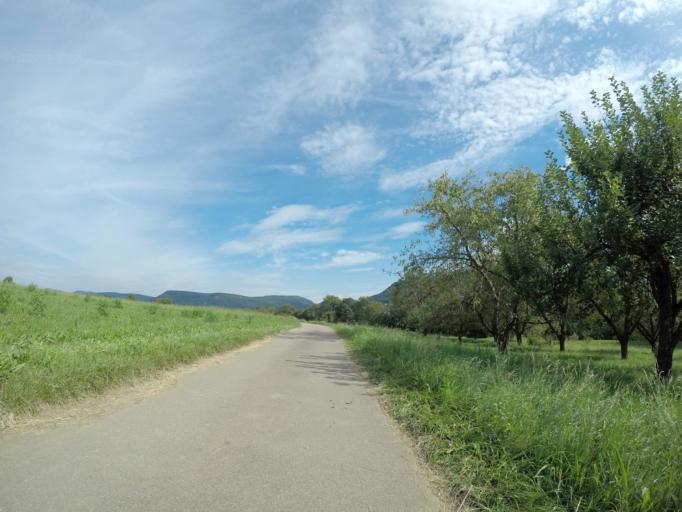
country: DE
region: Baden-Wuerttemberg
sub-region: Tuebingen Region
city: Pfullingen
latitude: 48.4550
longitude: 9.2012
